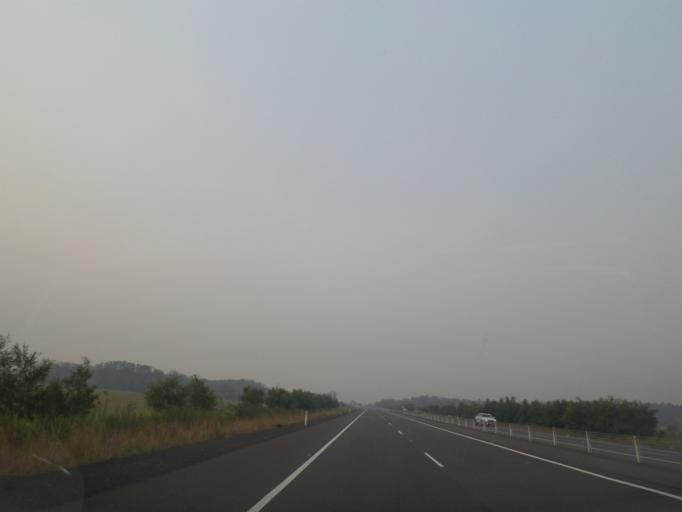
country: AU
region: New South Wales
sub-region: Nambucca Shire
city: Macksville
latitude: -30.7245
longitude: 152.9264
